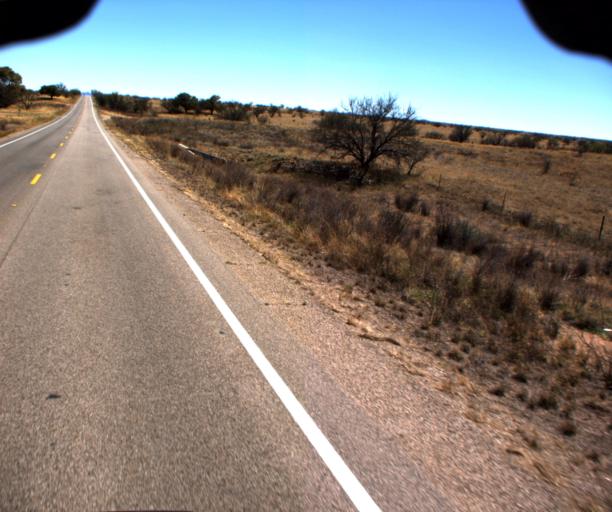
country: US
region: Arizona
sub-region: Pima County
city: Corona de Tucson
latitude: 31.7545
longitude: -110.6739
